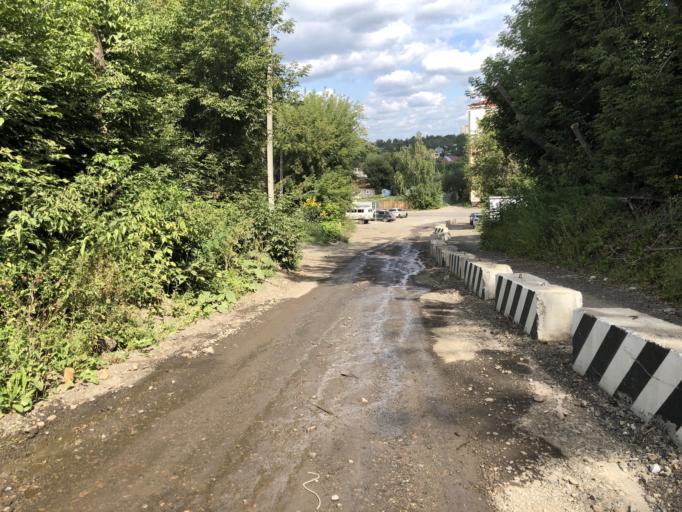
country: RU
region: Tomsk
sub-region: Tomskiy Rayon
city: Tomsk
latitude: 56.4808
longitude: 84.9621
